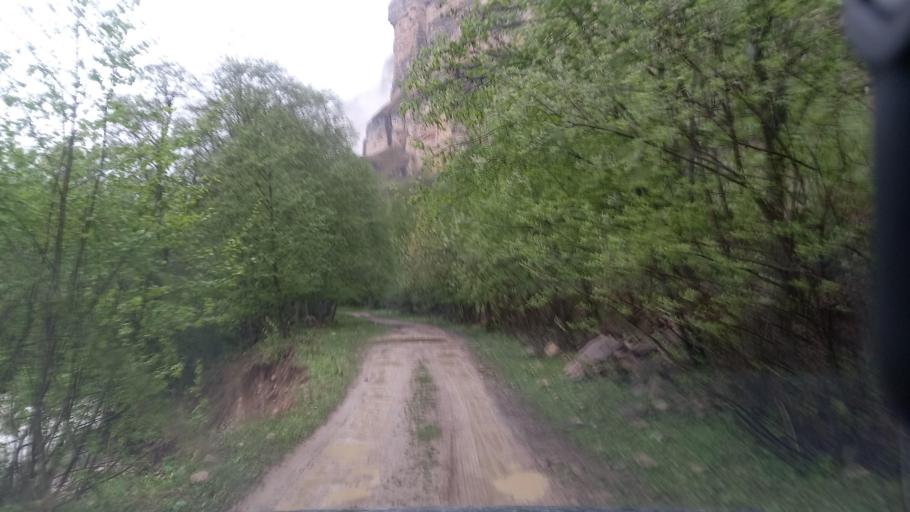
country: RU
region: Kabardino-Balkariya
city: Bylym
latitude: 43.5936
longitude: 42.9685
